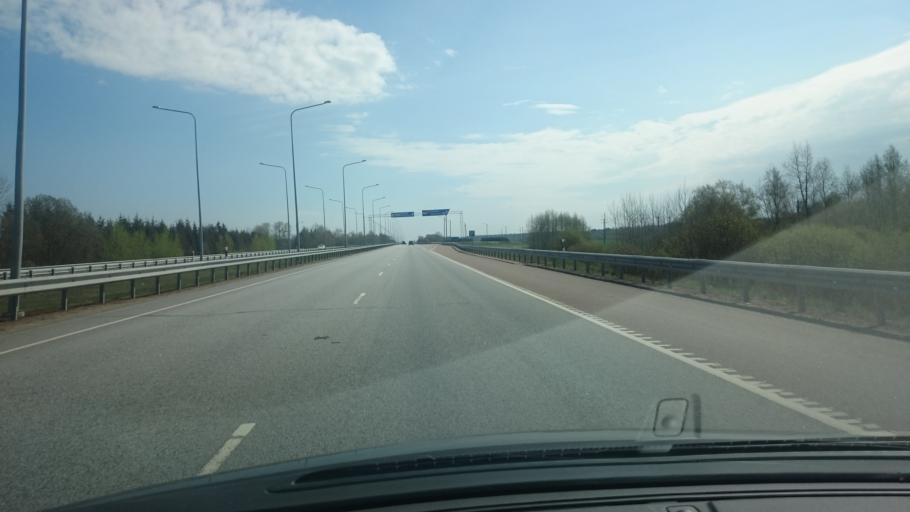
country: EE
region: Harju
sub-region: Kuusalu vald
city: Kuusalu
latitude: 59.4446
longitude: 25.3657
